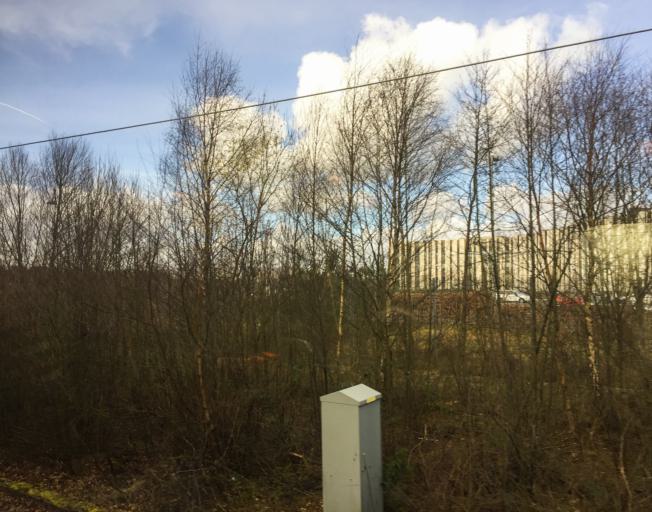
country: GB
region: Scotland
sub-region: North Lanarkshire
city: Glenboig
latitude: 55.8846
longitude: -4.0729
